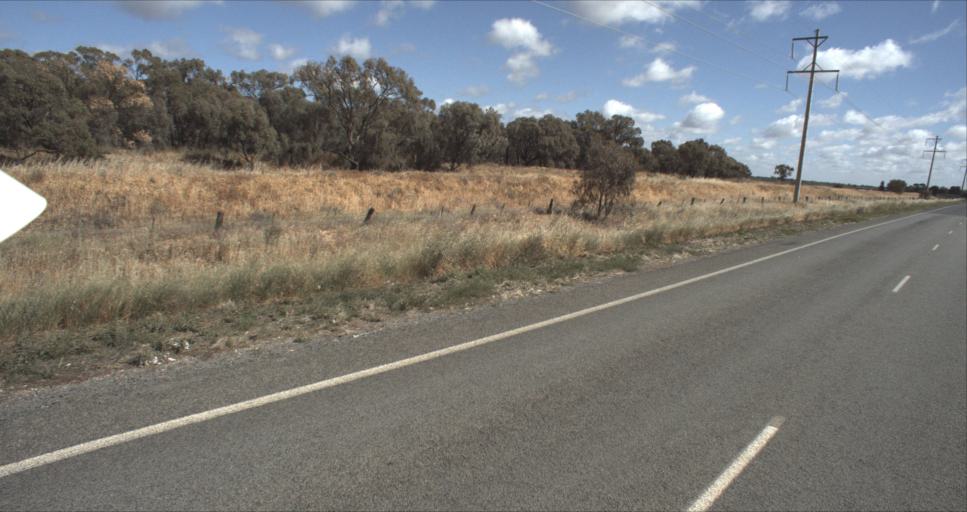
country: AU
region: New South Wales
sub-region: Murrumbidgee Shire
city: Darlington Point
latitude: -34.5446
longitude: 146.1715
